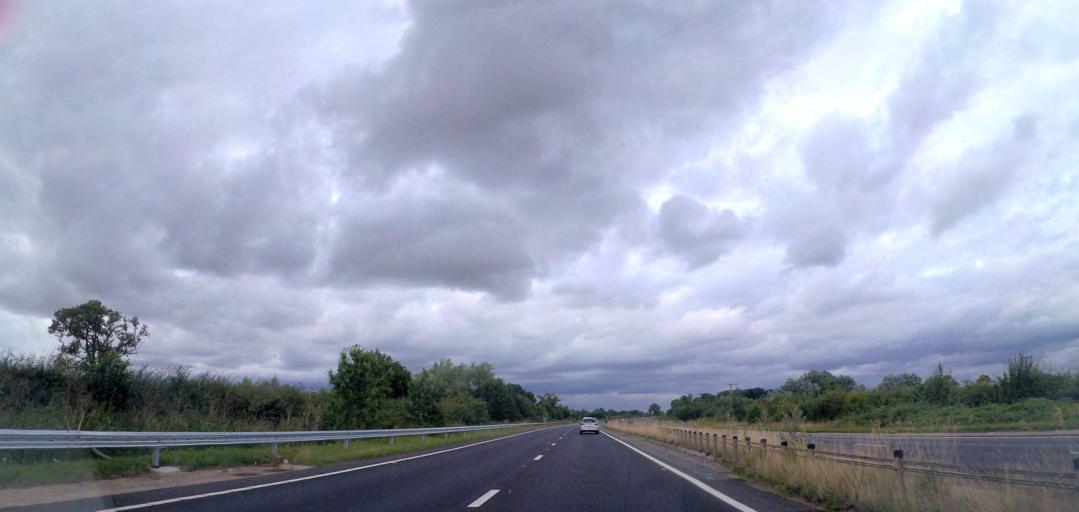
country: GB
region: England
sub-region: Norfolk
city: Snetterton
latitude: 52.4829
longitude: 0.9624
